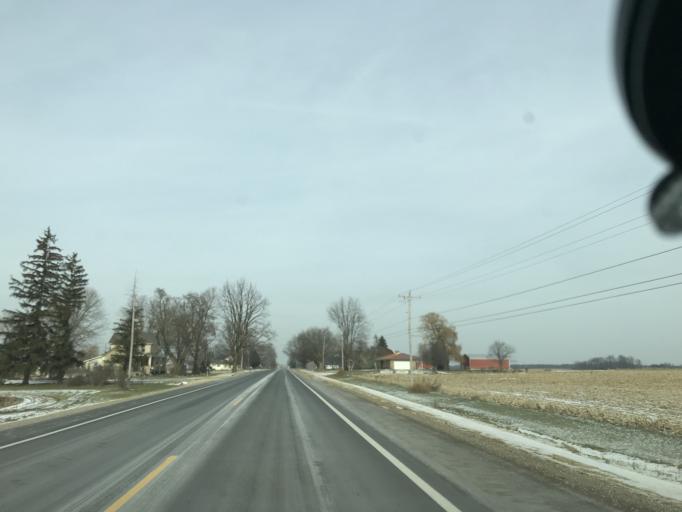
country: US
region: Michigan
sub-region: Ionia County
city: Lake Odessa
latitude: 42.8611
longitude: -85.0750
